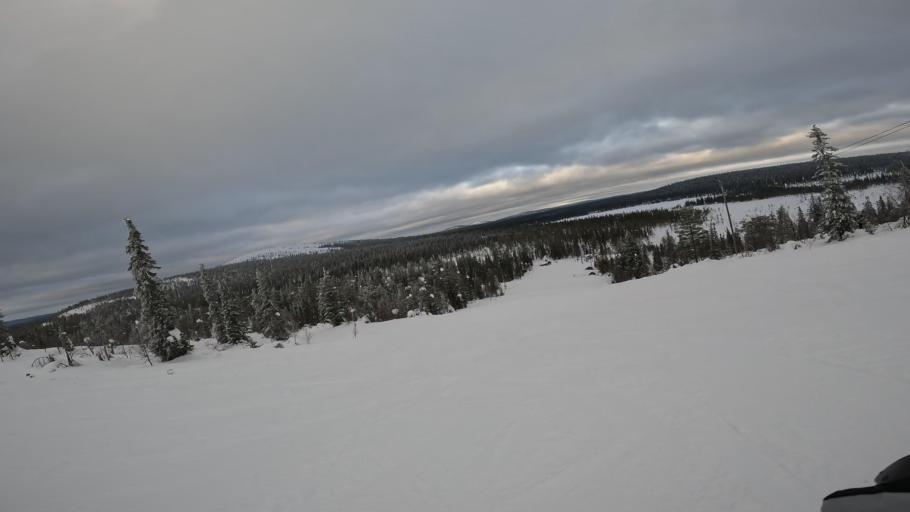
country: FI
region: Lapland
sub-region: Itae-Lappi
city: Salla
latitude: 66.7643
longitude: 28.7954
